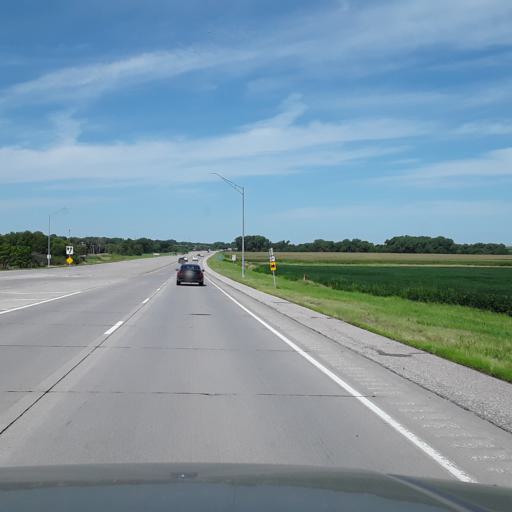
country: US
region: Nebraska
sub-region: Lancaster County
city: Lincoln
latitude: 40.8796
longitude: -96.7640
